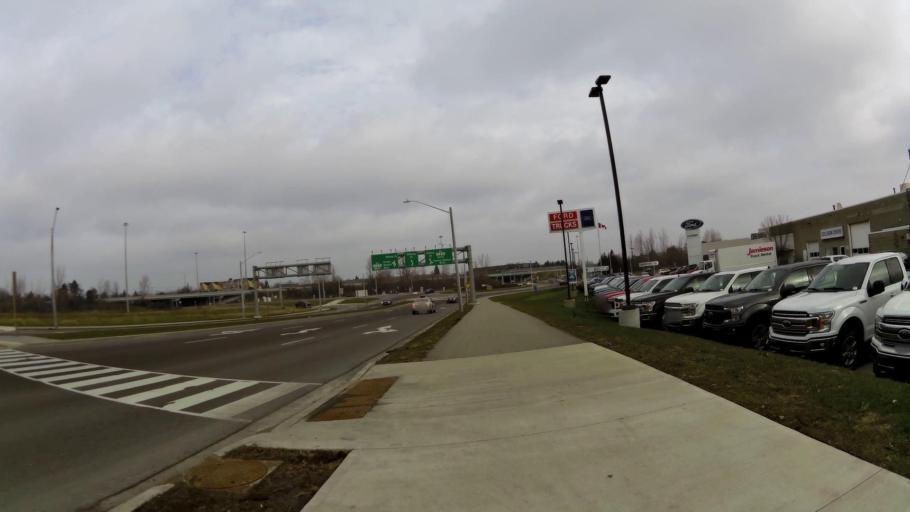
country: CA
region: Ontario
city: Kitchener
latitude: 43.4254
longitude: -80.4834
